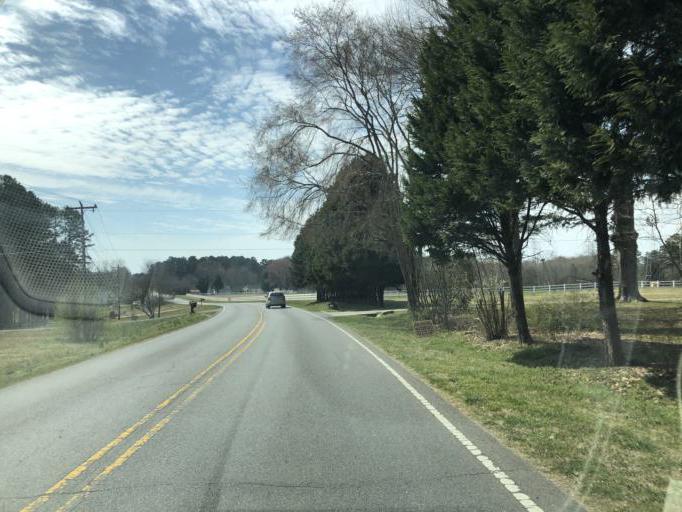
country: US
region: North Carolina
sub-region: Gaston County
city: Stanley
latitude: 35.3377
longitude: -81.1150
